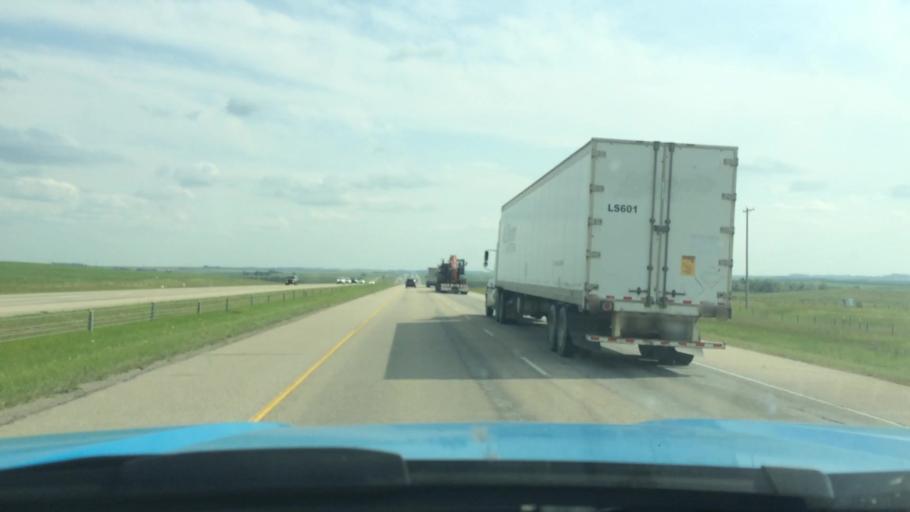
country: CA
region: Alberta
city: Carstairs
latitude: 51.5266
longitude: -114.0252
